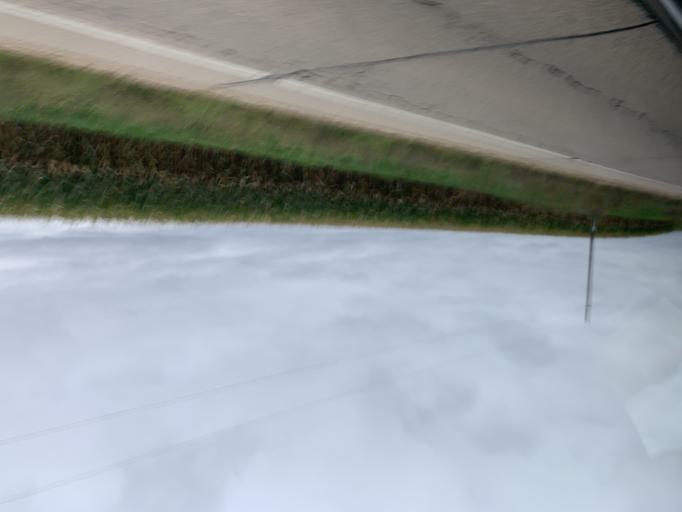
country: US
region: Wisconsin
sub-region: Grant County
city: Muscoda
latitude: 43.2198
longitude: -90.4910
